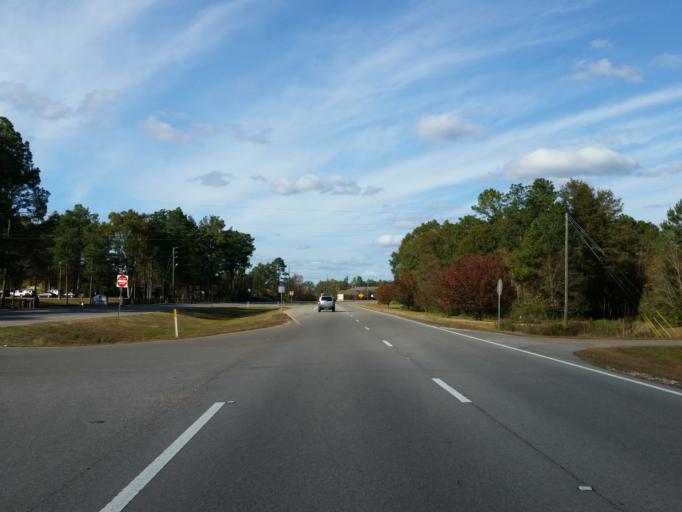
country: US
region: Mississippi
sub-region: Forrest County
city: Hattiesburg
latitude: 31.2937
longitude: -89.3234
